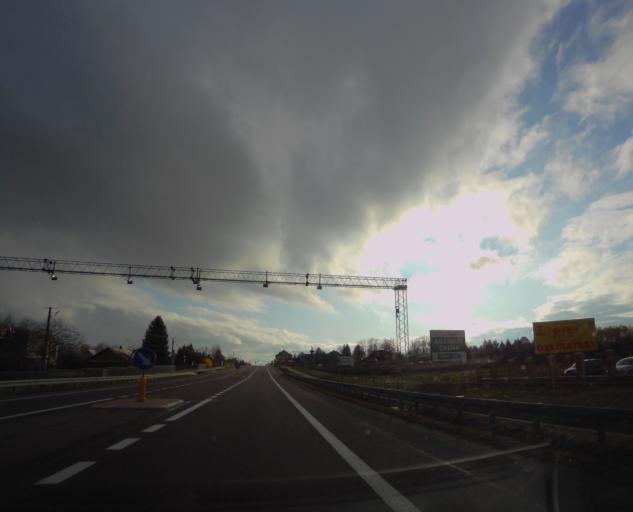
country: PL
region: Subcarpathian Voivodeship
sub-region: Powiat przemyski
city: Orly
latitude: 49.8780
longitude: 22.8131
